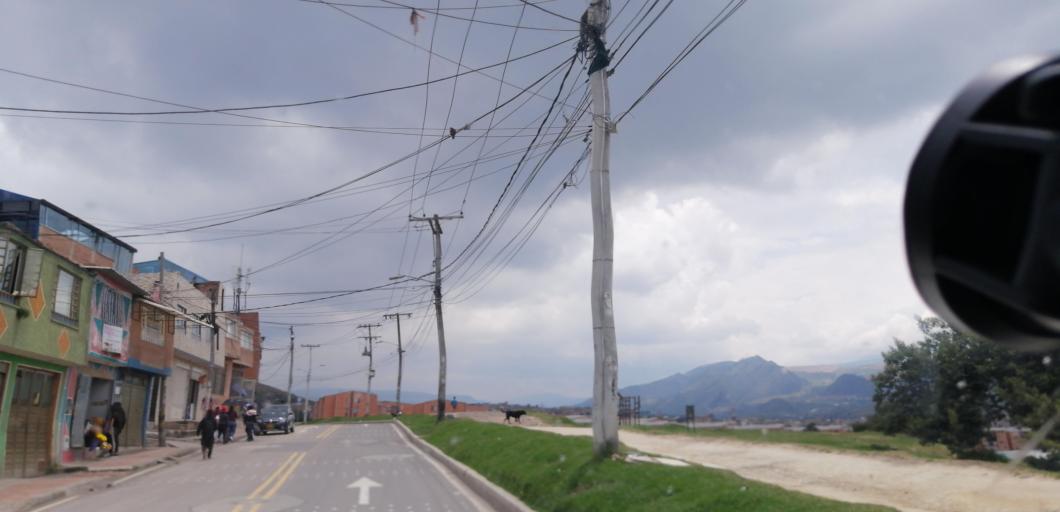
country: CO
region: Bogota D.C.
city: Bogota
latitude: 4.5338
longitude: -74.1156
